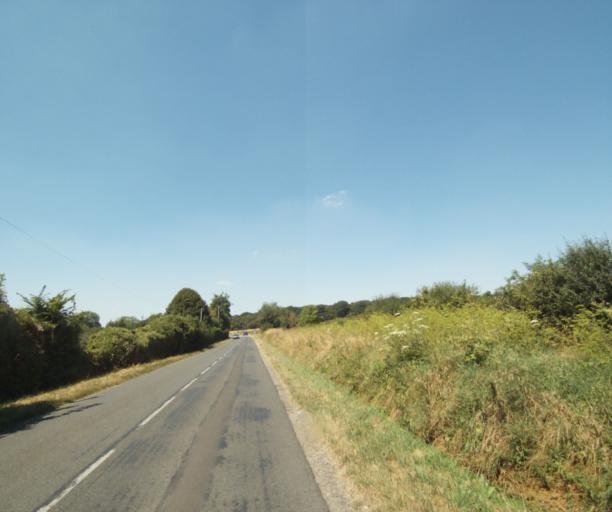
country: FR
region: Ile-de-France
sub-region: Departement de Seine-et-Marne
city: Chanteloup-en-Brie
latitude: 48.8555
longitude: 2.7297
